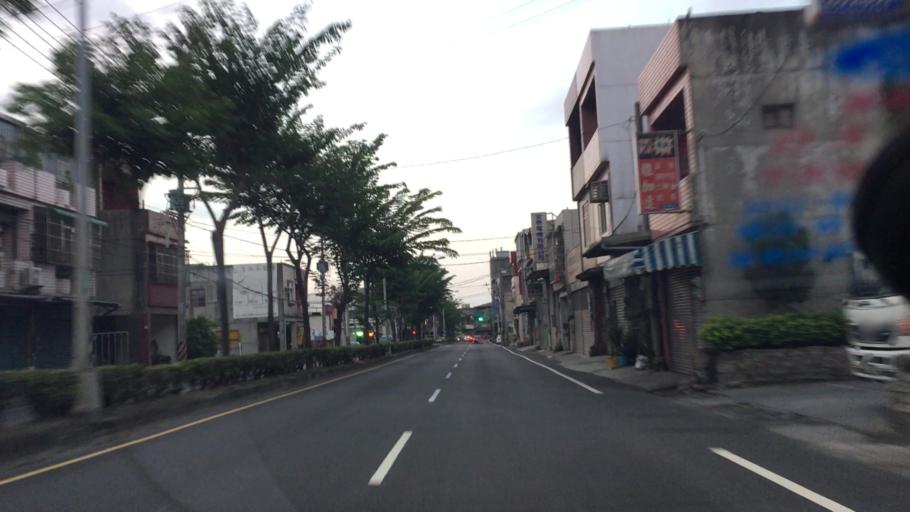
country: TW
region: Taiwan
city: Taoyuan City
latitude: 25.0604
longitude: 121.2673
